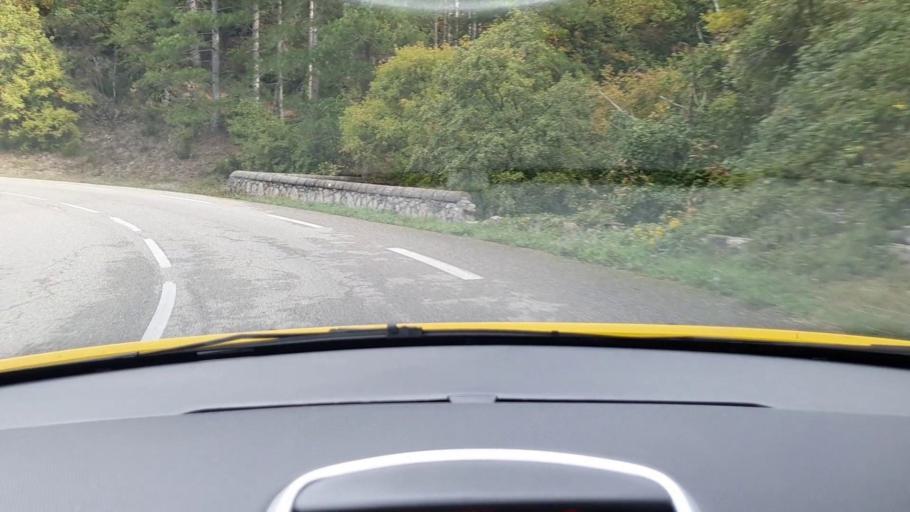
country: FR
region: Languedoc-Roussillon
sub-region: Departement du Gard
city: Le Vigan
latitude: 44.0192
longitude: 3.6016
